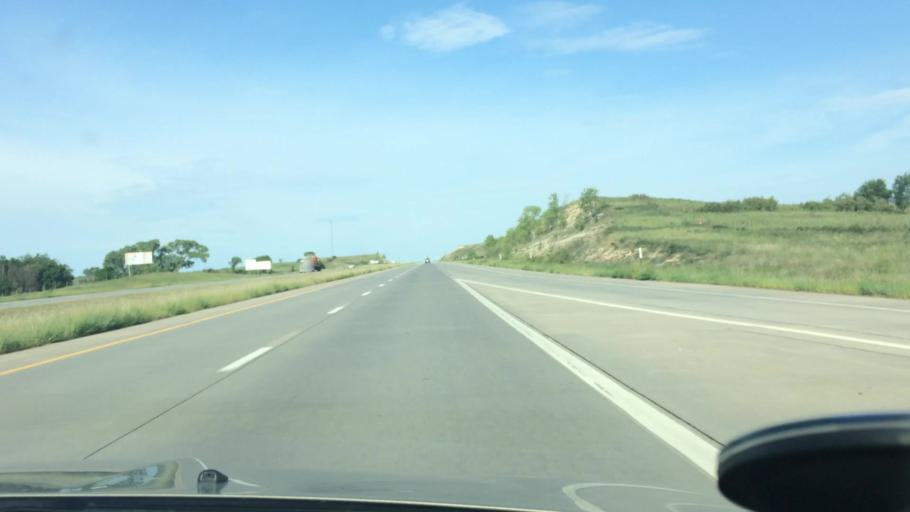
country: US
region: Kansas
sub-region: Riley County
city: Ogden
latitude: 39.0656
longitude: -96.6593
